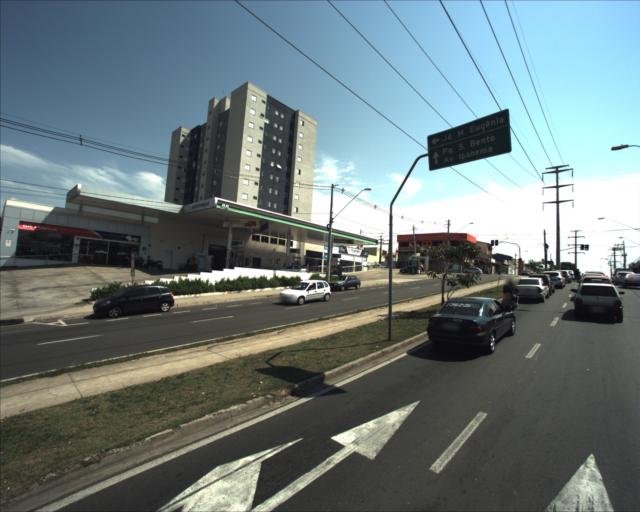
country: BR
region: Sao Paulo
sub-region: Sorocaba
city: Sorocaba
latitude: -23.4538
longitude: -47.4838
